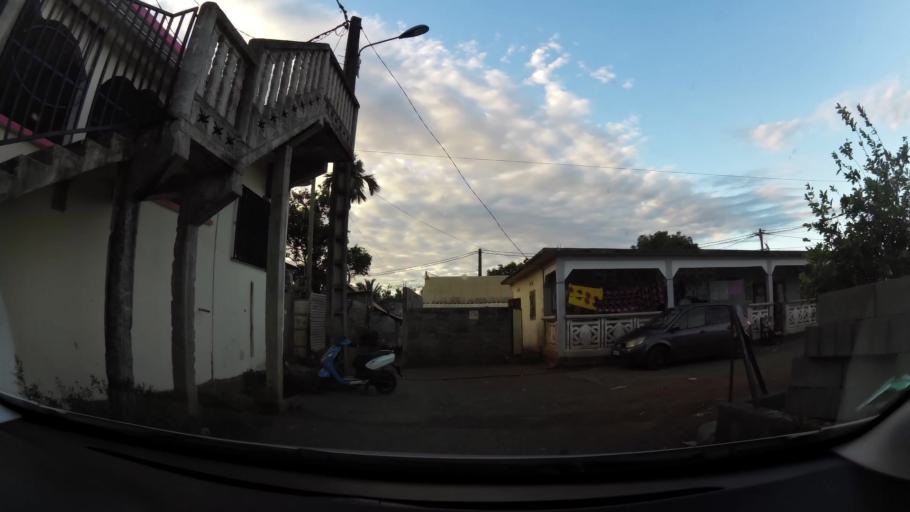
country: YT
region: Koungou
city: Koungou
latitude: -12.7304
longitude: 45.1866
